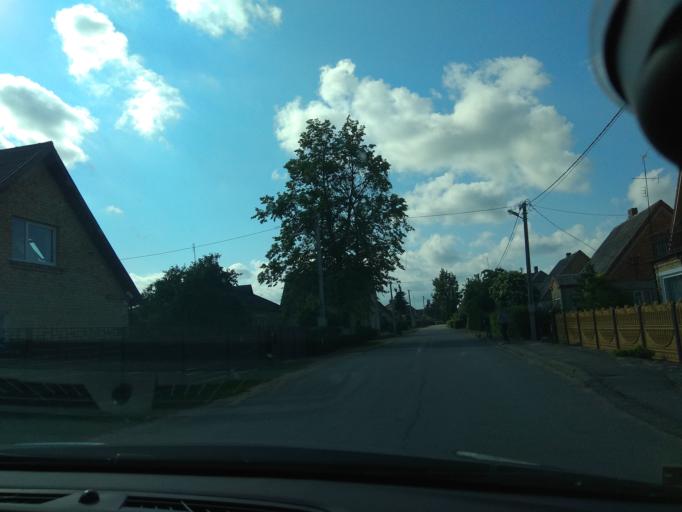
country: LT
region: Siauliu apskritis
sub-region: Joniskis
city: Joniskis
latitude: 56.2459
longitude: 23.6244
